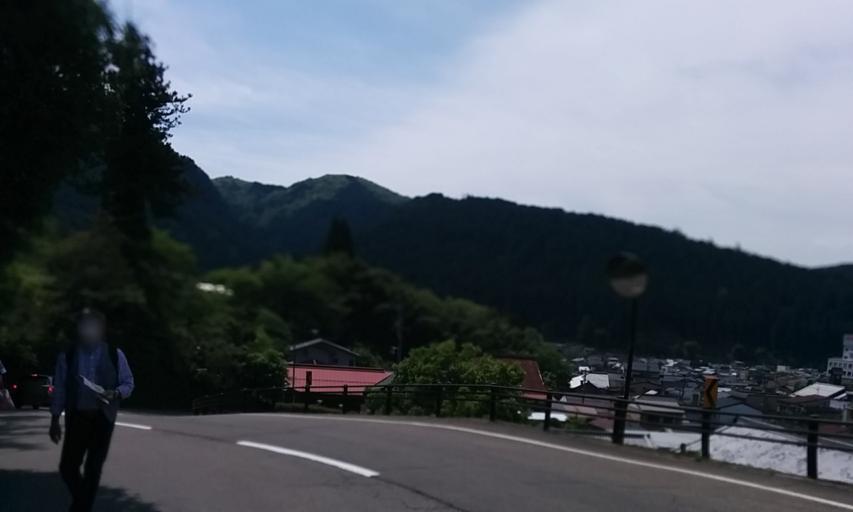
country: JP
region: Gifu
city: Gujo
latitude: 35.7524
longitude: 136.9587
